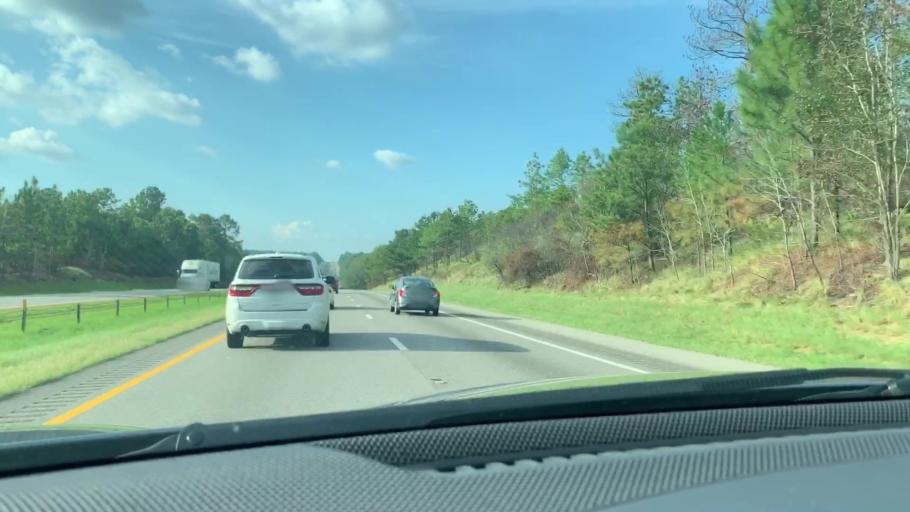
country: US
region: South Carolina
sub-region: Calhoun County
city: Oak Grove
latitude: 33.7168
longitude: -80.9236
